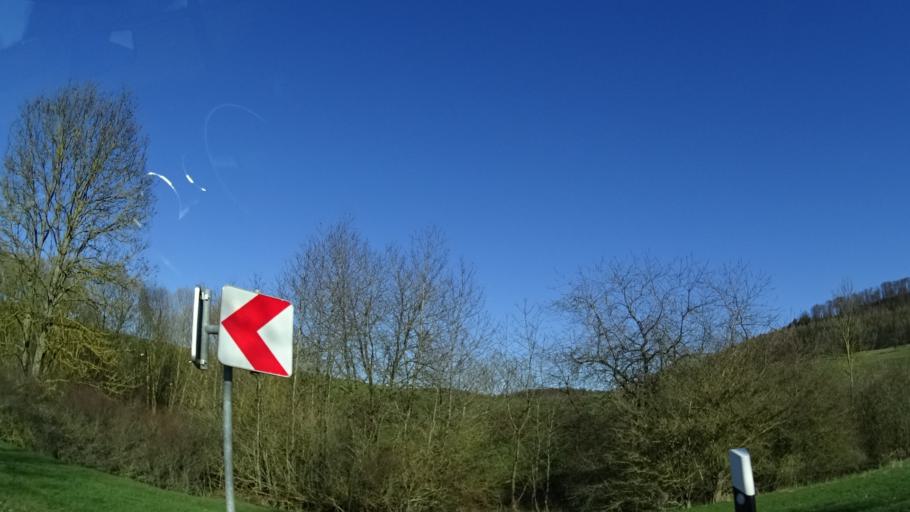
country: DE
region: Thuringia
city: Stepfershausen
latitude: 50.5480
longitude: 10.2854
